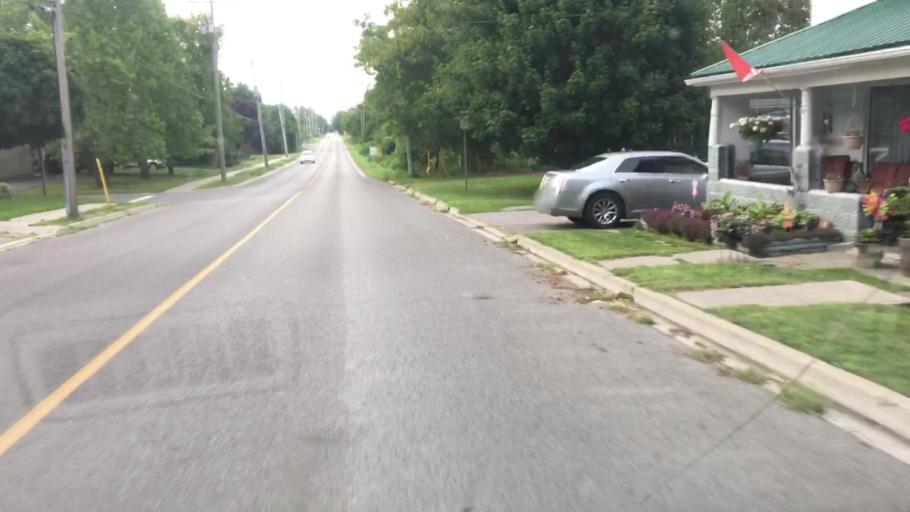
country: CA
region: Ontario
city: Quinte West
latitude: 44.0386
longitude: -77.7461
